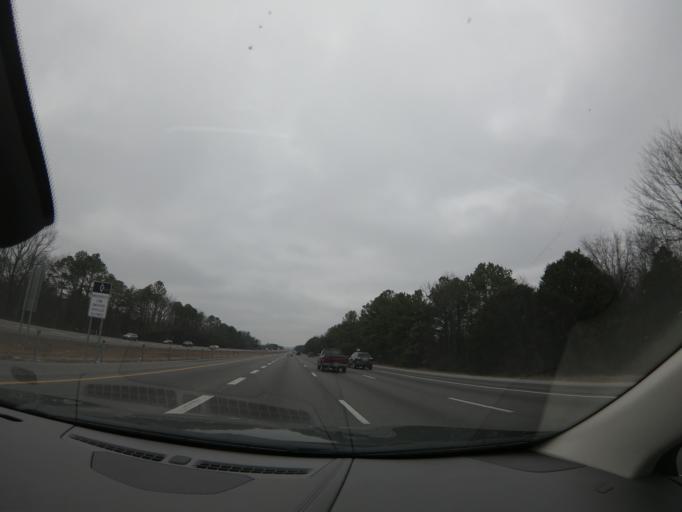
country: US
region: Tennessee
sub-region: Rutherford County
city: Smyrna
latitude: 35.9047
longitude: -86.4983
